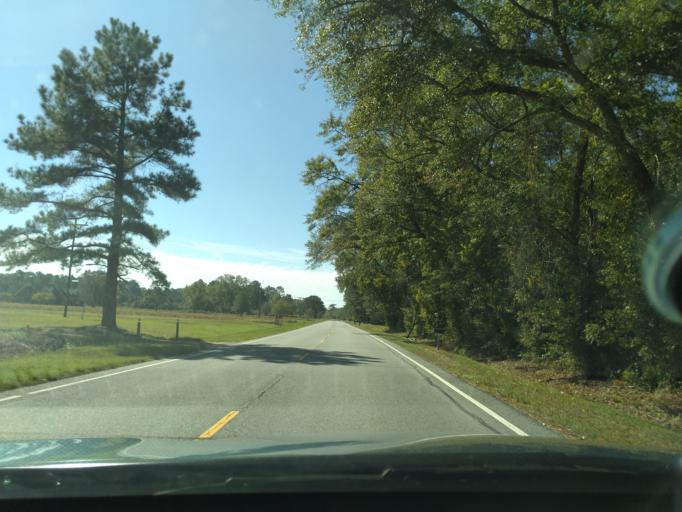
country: US
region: North Carolina
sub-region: Beaufort County
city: Belhaven
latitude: 35.6434
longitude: -76.8018
